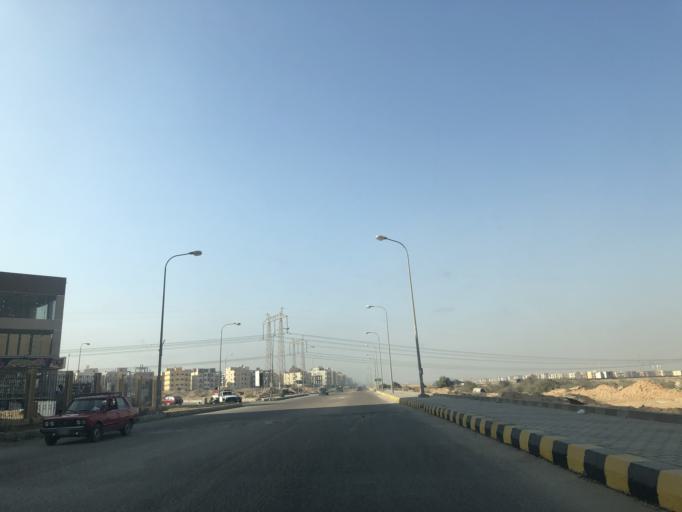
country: EG
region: Al Jizah
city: Madinat Sittah Uktubar
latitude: 29.9207
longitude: 31.0557
